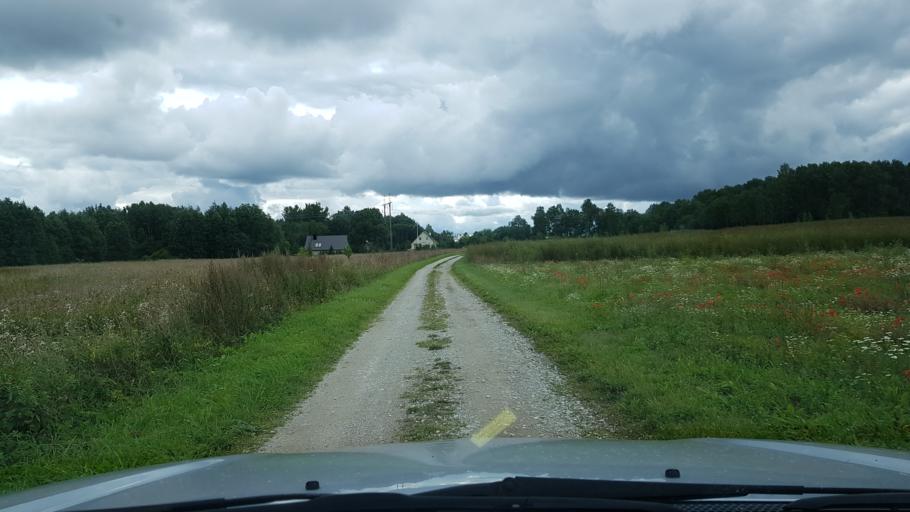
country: EE
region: Harju
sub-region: Raasiku vald
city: Arukula
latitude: 59.2721
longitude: 25.1059
